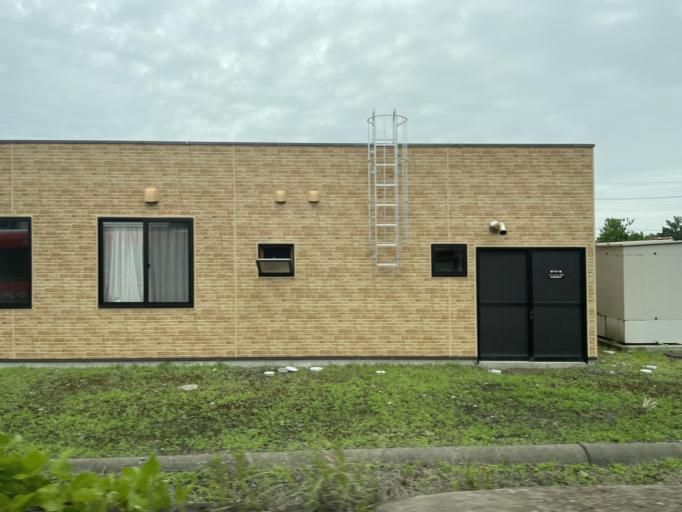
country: JP
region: Akita
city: Tenno
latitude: 39.8884
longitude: 139.8506
